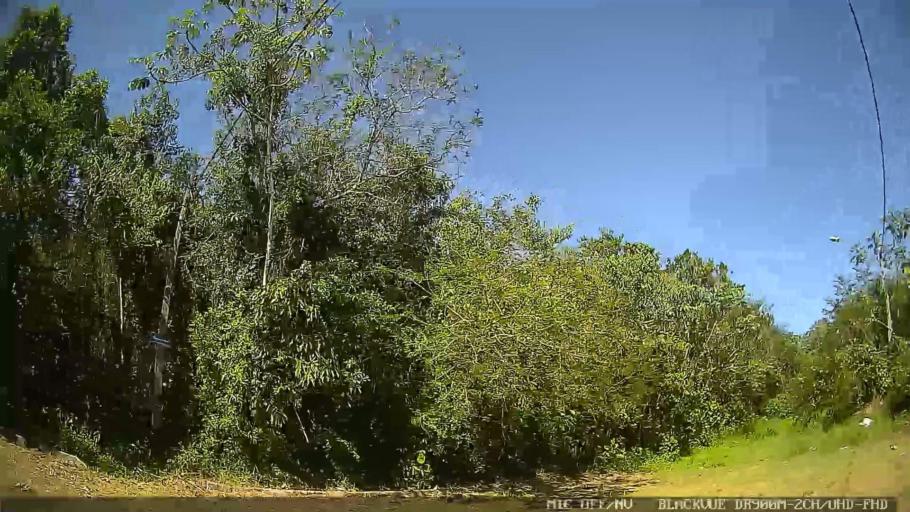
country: BR
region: Sao Paulo
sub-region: Iguape
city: Iguape
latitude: -24.6930
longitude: -47.5605
